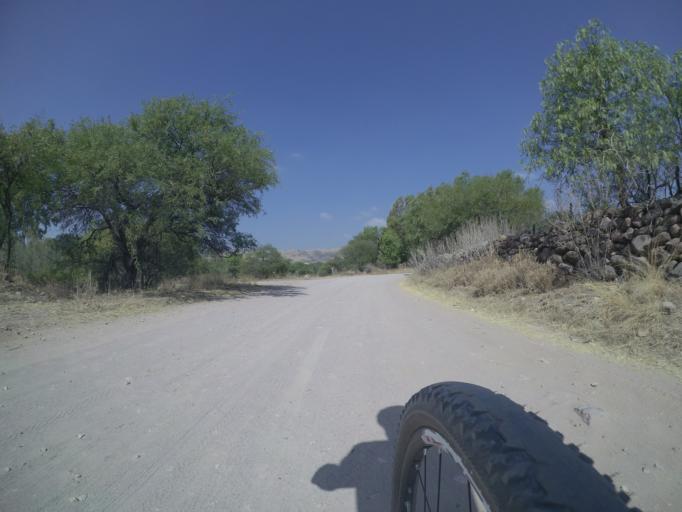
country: MX
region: Aguascalientes
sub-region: Jesus Maria
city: Paseos de las Haciendas [Fraccionamiento]
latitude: 21.9978
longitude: -102.3553
